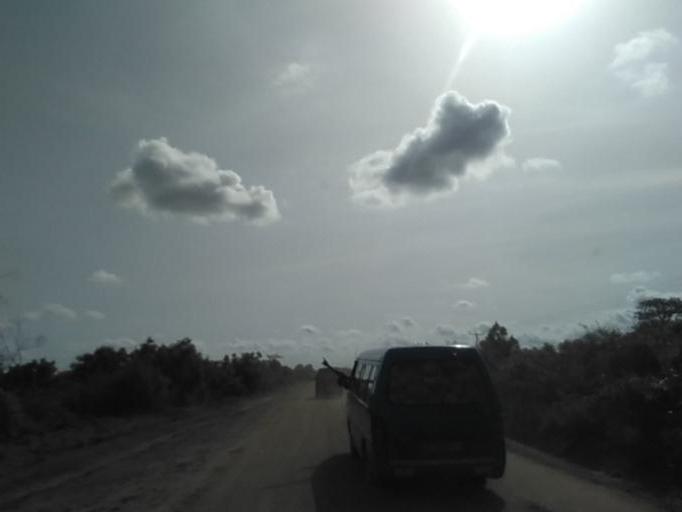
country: GH
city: Akropong
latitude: 6.0333
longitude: 0.3277
